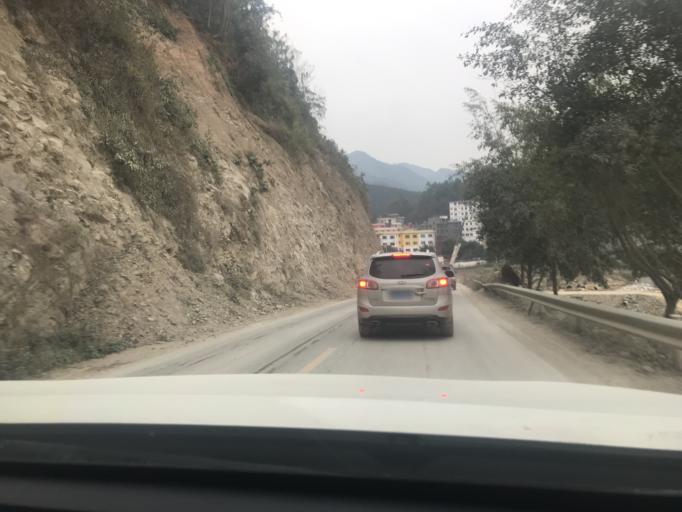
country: CN
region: Guangxi Zhuangzu Zizhiqu
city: Xinzhou
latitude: 24.9858
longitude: 105.8189
